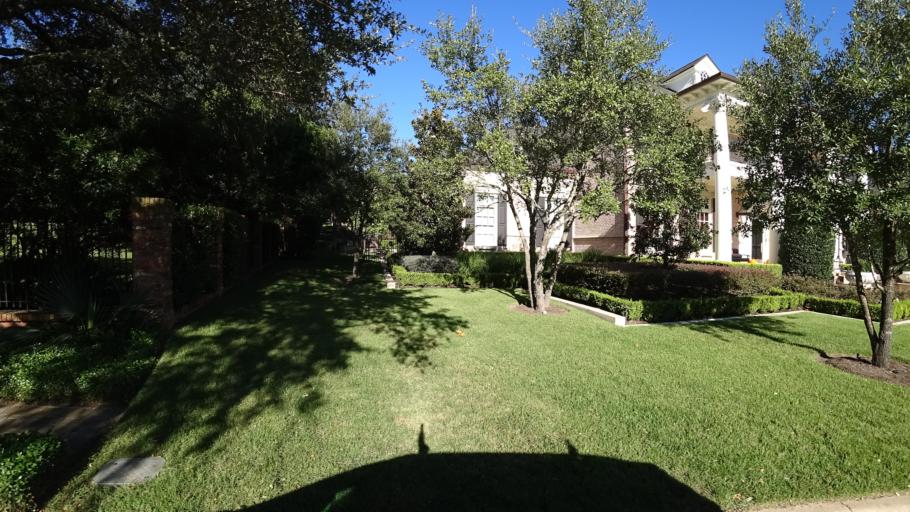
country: US
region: Texas
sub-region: Travis County
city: West Lake Hills
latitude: 30.3371
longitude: -97.7994
